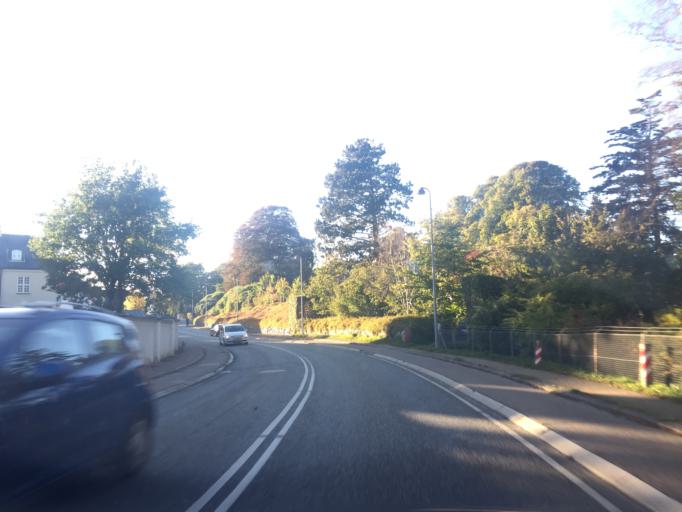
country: DK
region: Capital Region
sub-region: Gladsaxe Municipality
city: Buddinge
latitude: 55.7746
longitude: 12.4674
